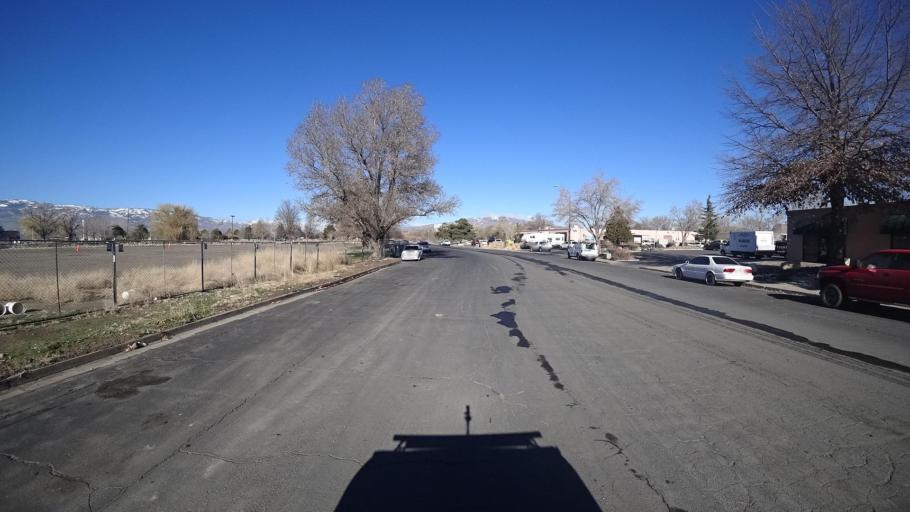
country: US
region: Nevada
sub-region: Washoe County
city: Sparks
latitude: 39.5153
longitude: -119.7498
